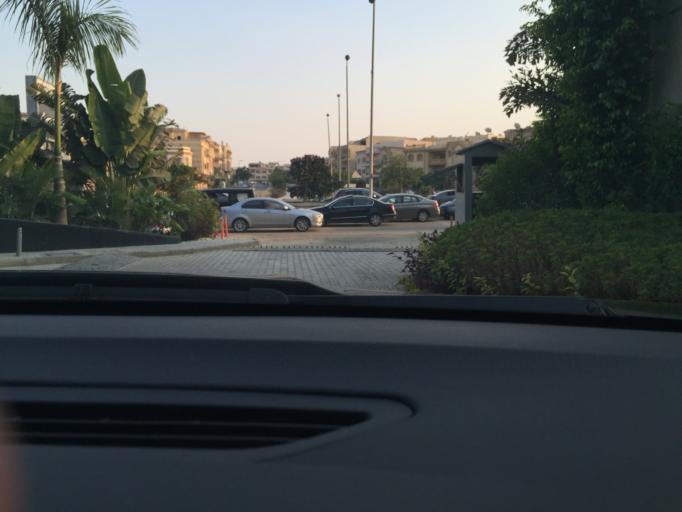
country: EG
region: Muhafazat al Qahirah
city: Cairo
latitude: 30.0168
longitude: 31.4212
